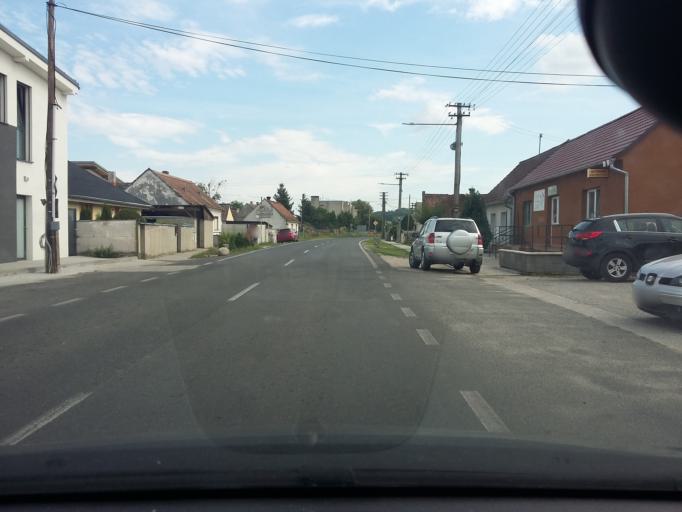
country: SK
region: Trnavsky
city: Gbely
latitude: 48.6270
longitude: 17.2046
